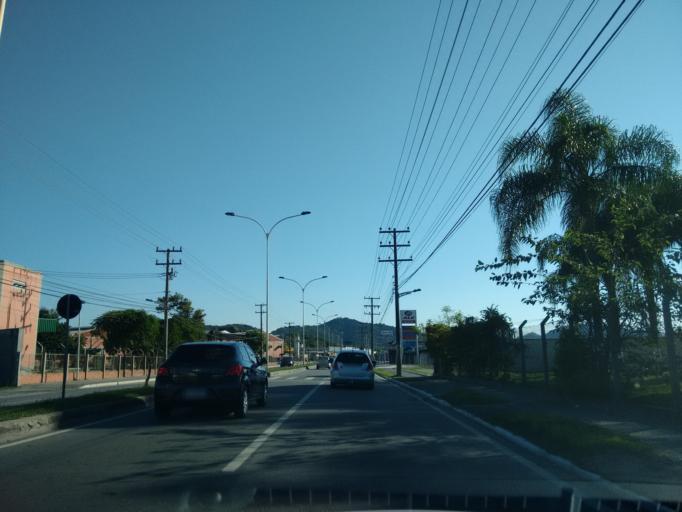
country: BR
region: Santa Catarina
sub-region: Itajai
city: Itajai
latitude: -26.8893
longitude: -48.7089
